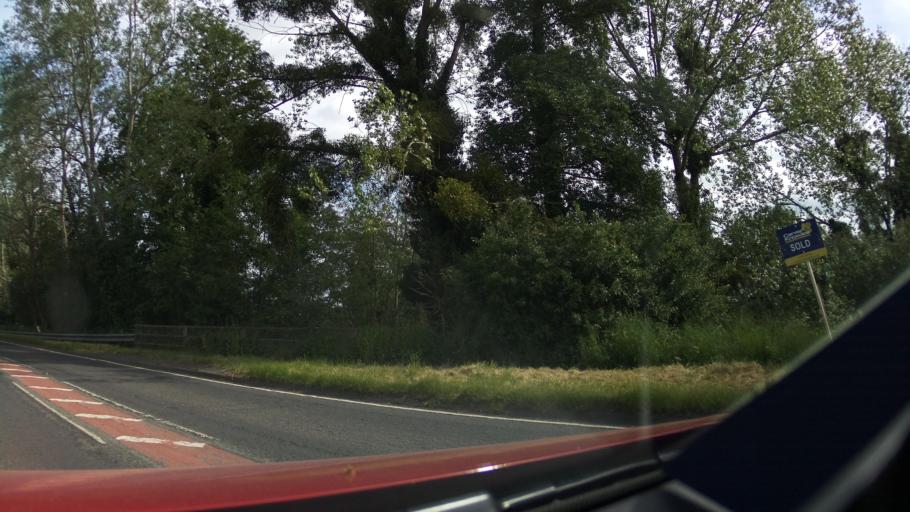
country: GB
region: England
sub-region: Worcestershire
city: Pershore
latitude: 52.1408
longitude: -2.1355
